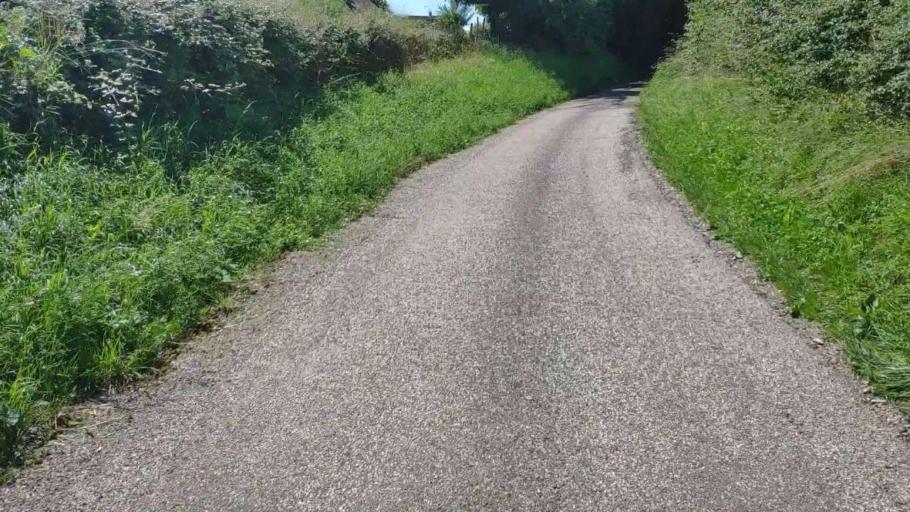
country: FR
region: Franche-Comte
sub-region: Departement du Jura
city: Poligny
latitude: 46.8324
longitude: 5.5652
